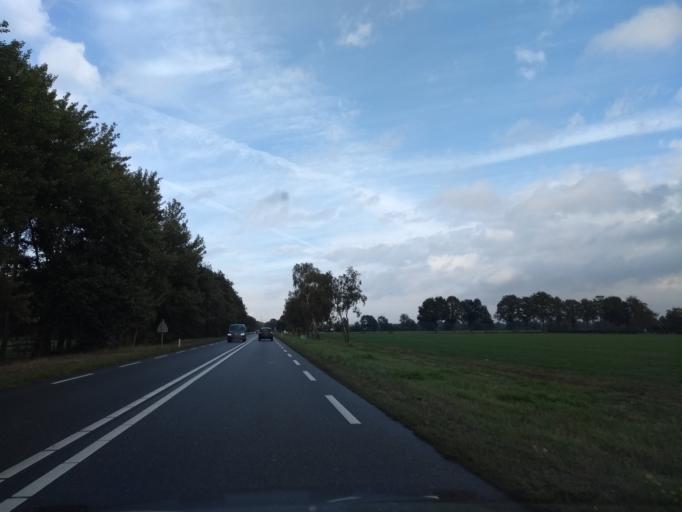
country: NL
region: Gelderland
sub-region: Oost Gelre
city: Lichtenvoorde
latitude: 51.9838
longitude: 6.5466
